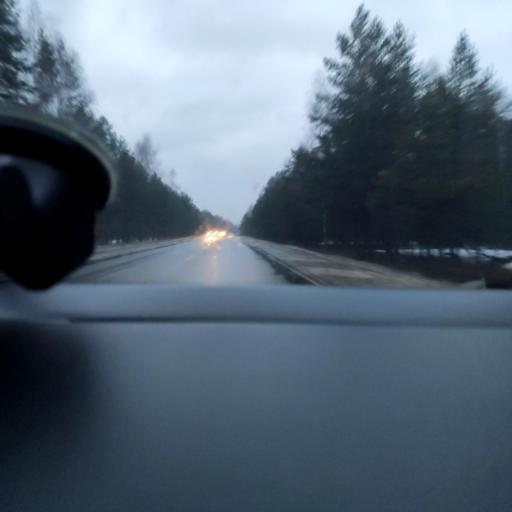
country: RU
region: Moskovskaya
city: Krasnyy Tkach
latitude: 55.4088
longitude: 39.1614
